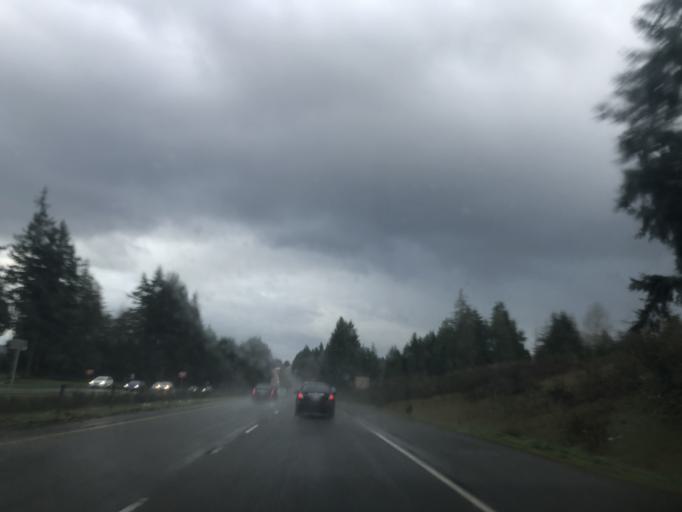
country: US
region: Washington
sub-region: Pierce County
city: Gig Harbor
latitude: 47.3345
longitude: -122.6030
